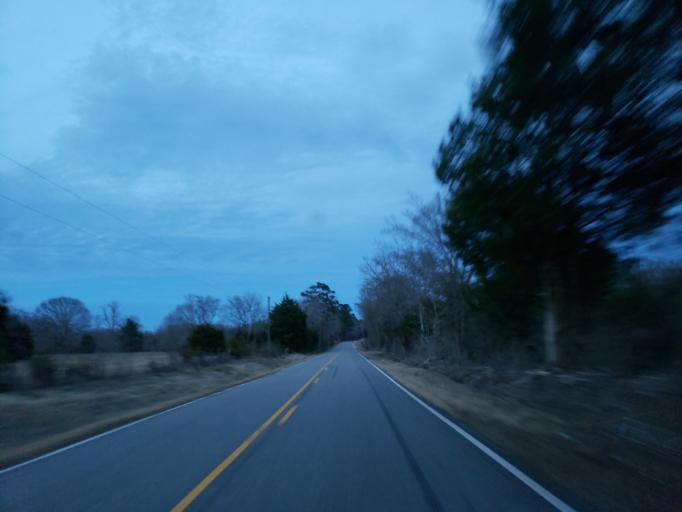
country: US
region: Alabama
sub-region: Greene County
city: Eutaw
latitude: 32.8799
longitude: -88.0715
